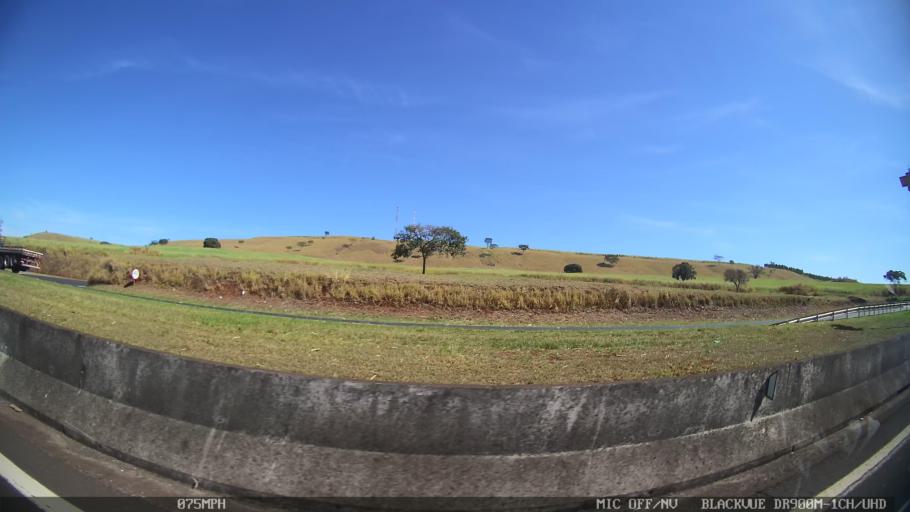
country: BR
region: Sao Paulo
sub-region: Sao Simao
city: Sao Simao
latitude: -21.4680
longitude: -47.6412
